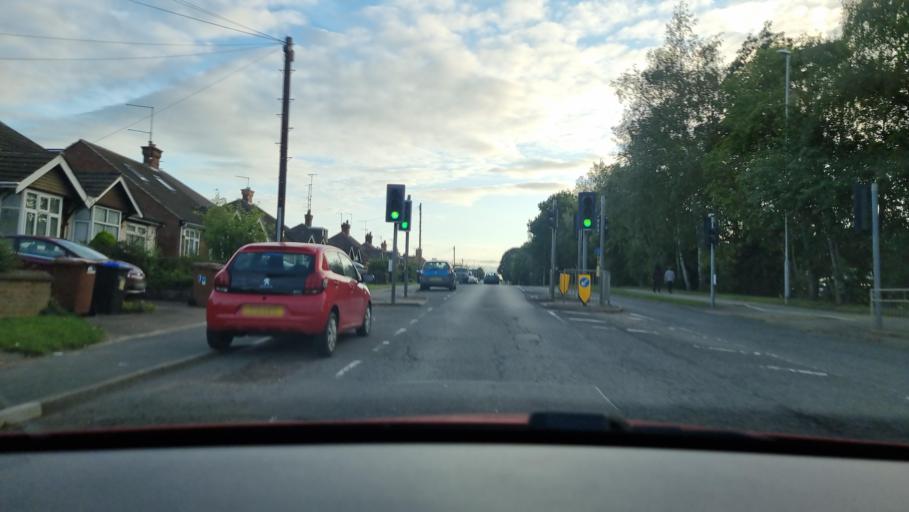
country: GB
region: England
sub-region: Northamptonshire
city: Northampton
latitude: 52.2452
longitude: -0.9298
